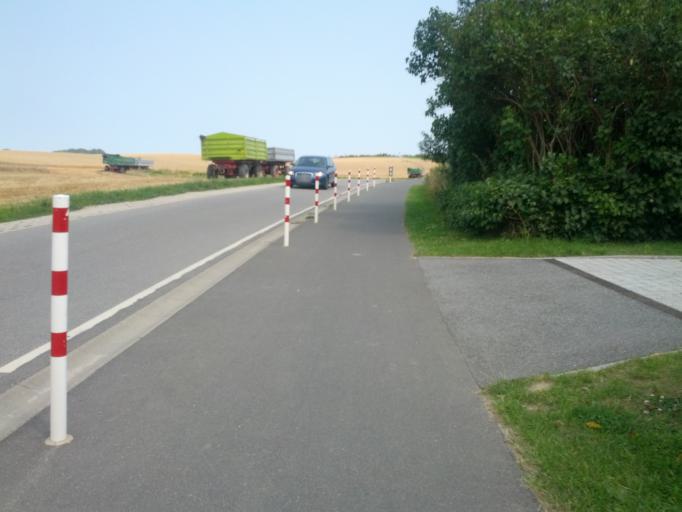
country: DE
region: Mecklenburg-Vorpommern
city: Bastorf
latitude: 54.1285
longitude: 11.6532
